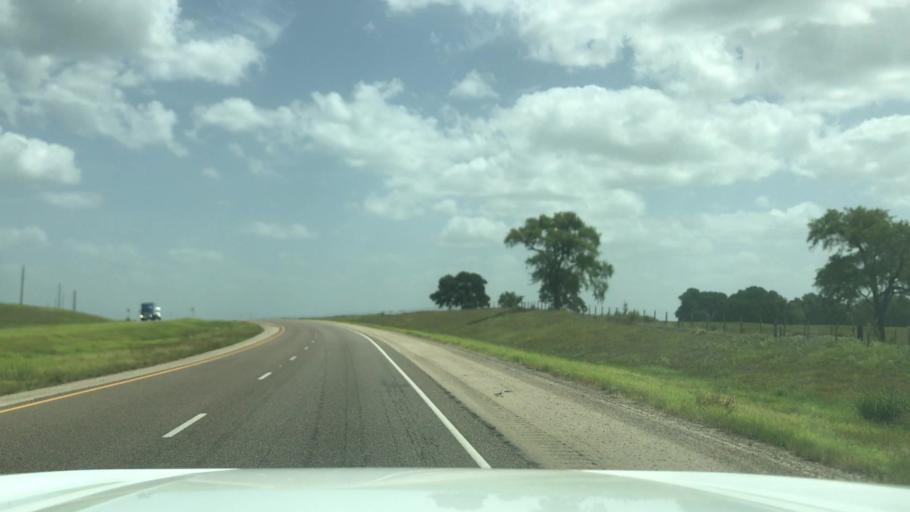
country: US
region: Texas
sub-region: Robertson County
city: Calvert
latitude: 31.0092
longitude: -96.7023
